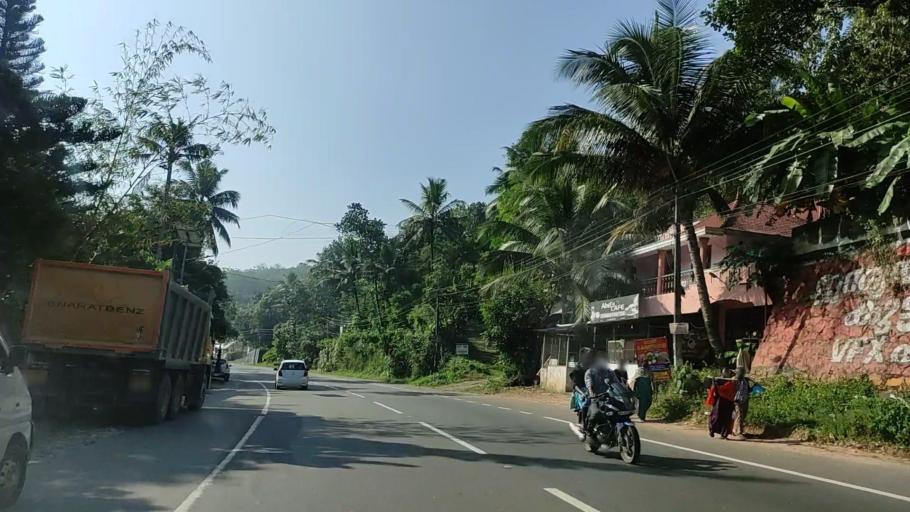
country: IN
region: Kerala
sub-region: Kollam
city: Punalur
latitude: 8.9143
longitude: 76.8532
